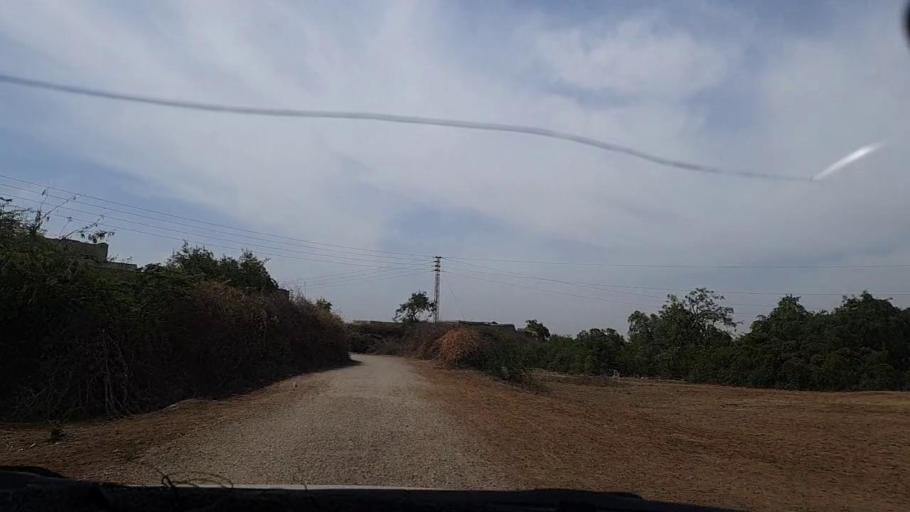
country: PK
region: Sindh
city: Dhoro Naro
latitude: 25.4356
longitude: 69.5078
